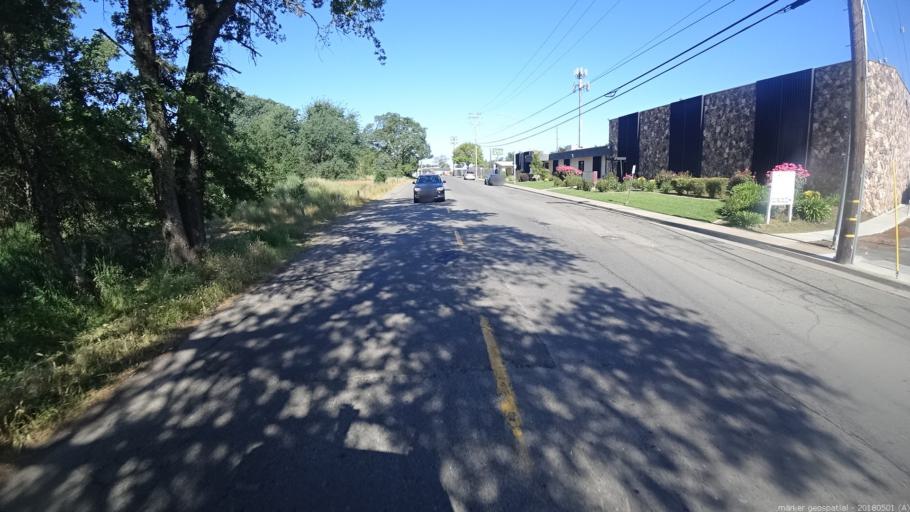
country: US
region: California
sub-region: Sacramento County
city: Arden-Arcade
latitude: 38.6433
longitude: -121.3865
